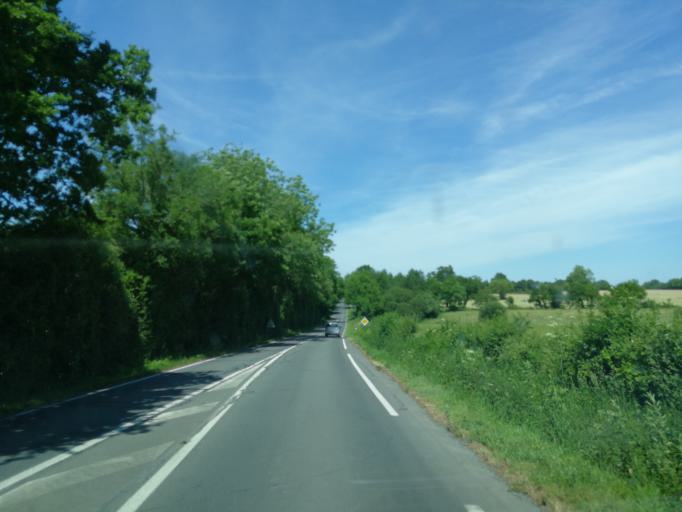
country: FR
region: Pays de la Loire
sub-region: Departement de la Vendee
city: Saint-Pierre-du-Chemin
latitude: 46.7224
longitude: -0.6766
